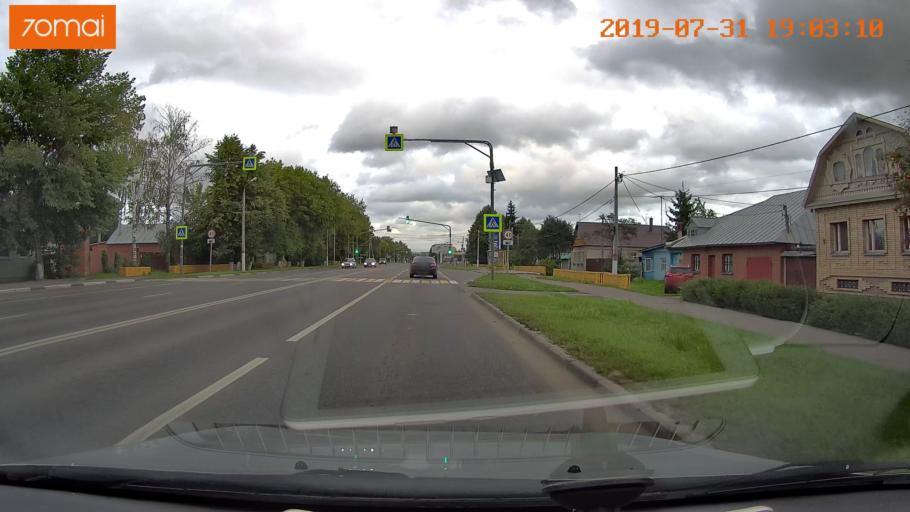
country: RU
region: Moskovskaya
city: Raduzhnyy
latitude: 55.1165
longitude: 38.7363
